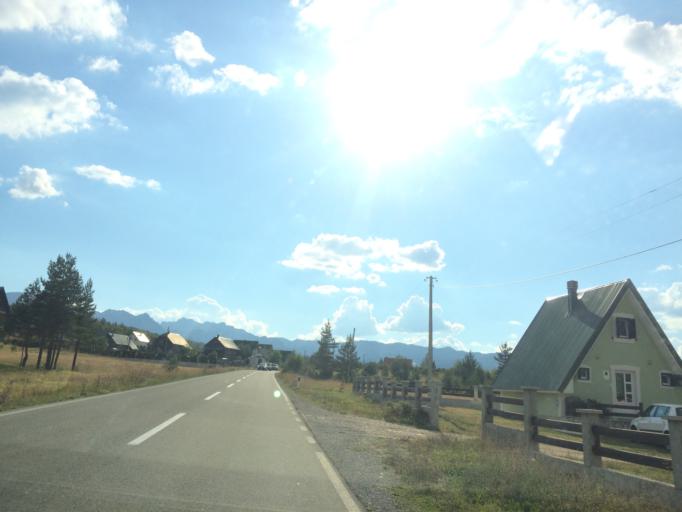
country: ME
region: Opstina Zabljak
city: Zabljak
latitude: 43.1650
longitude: 19.1777
